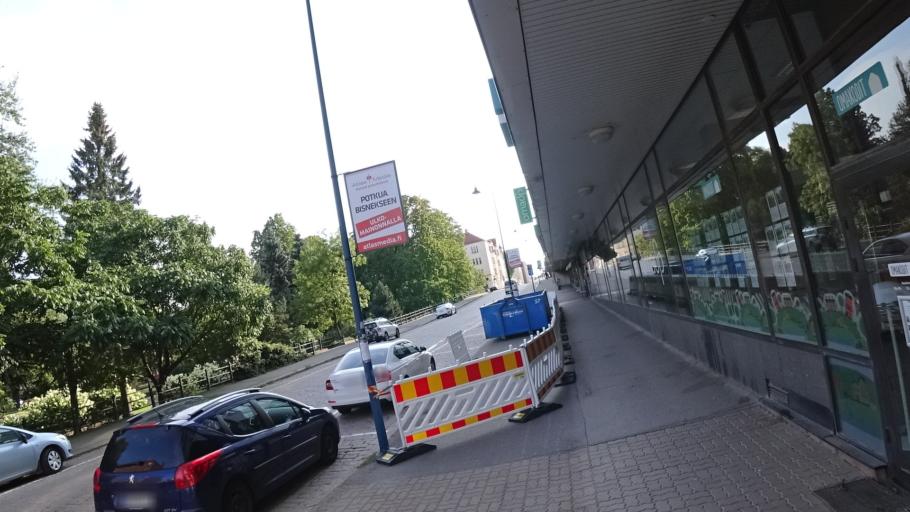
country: FI
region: Kymenlaakso
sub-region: Kotka-Hamina
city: Kotka
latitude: 60.4665
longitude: 26.9420
